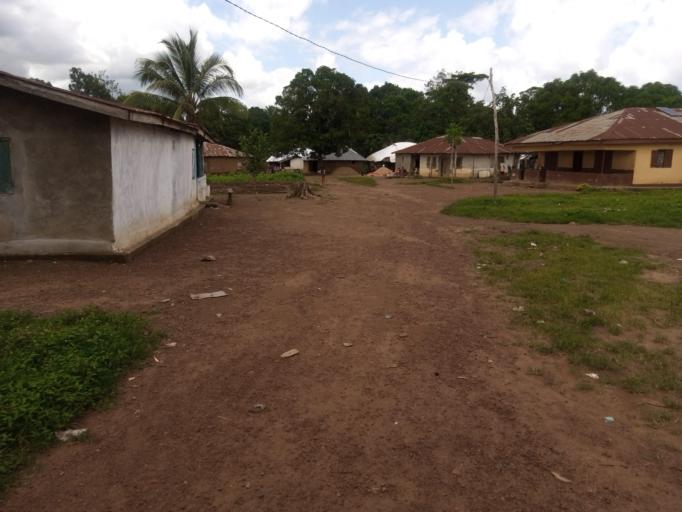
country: SL
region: Northern Province
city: Port Loko
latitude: 8.7784
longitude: -12.7703
